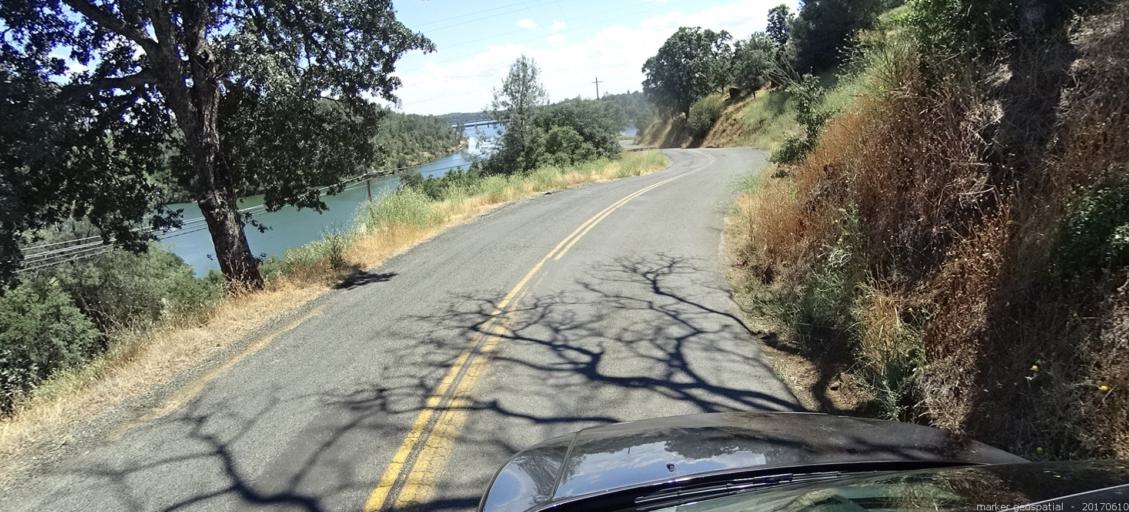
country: US
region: California
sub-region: Butte County
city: Oroville
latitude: 39.5471
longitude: -121.5418
